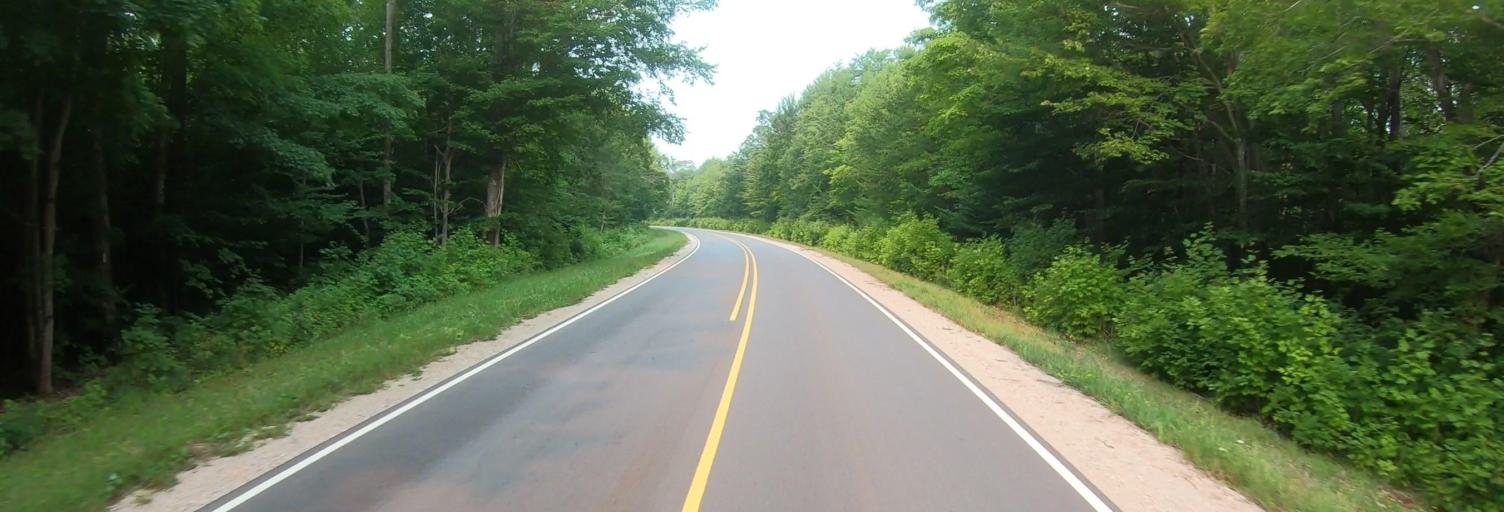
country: US
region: Michigan
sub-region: Luce County
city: Newberry
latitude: 46.4859
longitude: -85.0468
